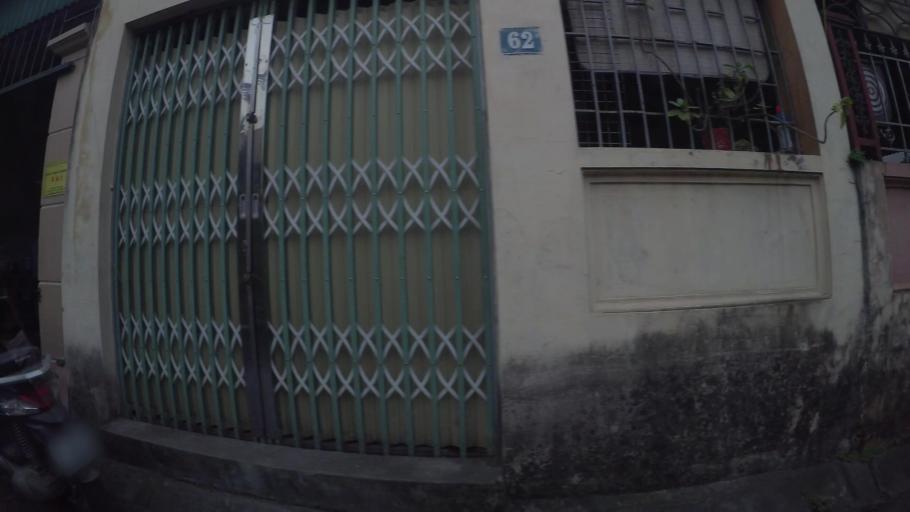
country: VN
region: Hung Yen
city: Van Giang
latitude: 20.9790
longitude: 105.8947
